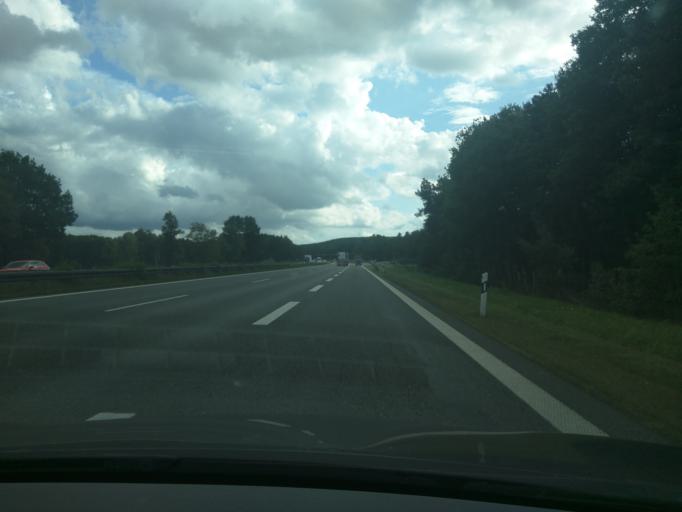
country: DE
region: Bavaria
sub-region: Upper Palatinate
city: Schwarzenfeld
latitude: 49.3480
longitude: 12.1500
